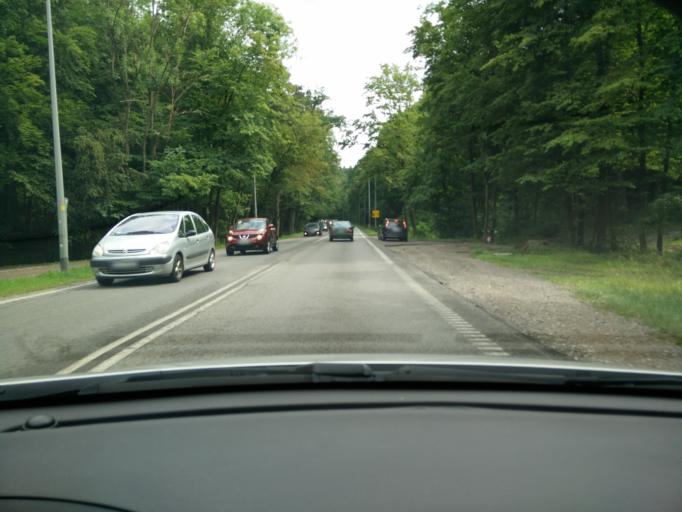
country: PL
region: Pomeranian Voivodeship
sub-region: Gdynia
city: Wielki Kack
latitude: 54.4274
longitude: 18.5022
